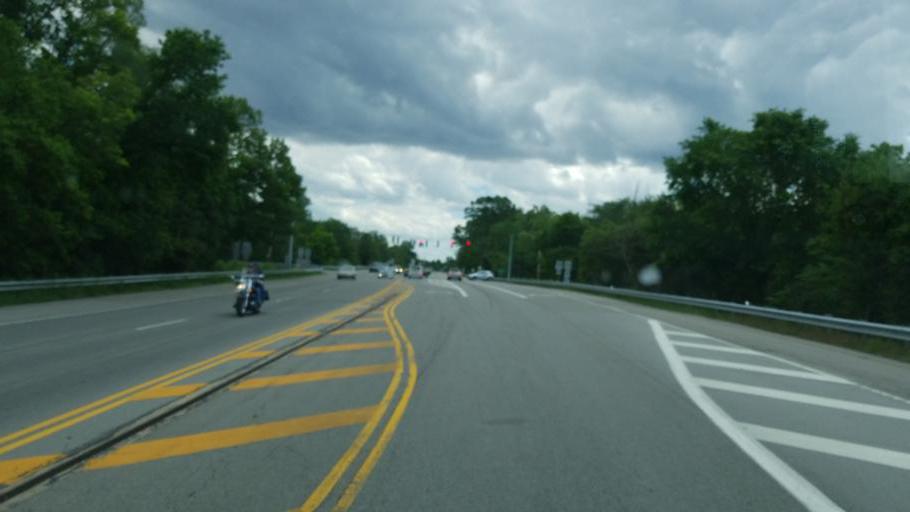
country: US
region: Ohio
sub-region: Erie County
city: Milan
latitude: 41.2970
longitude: -82.6098
